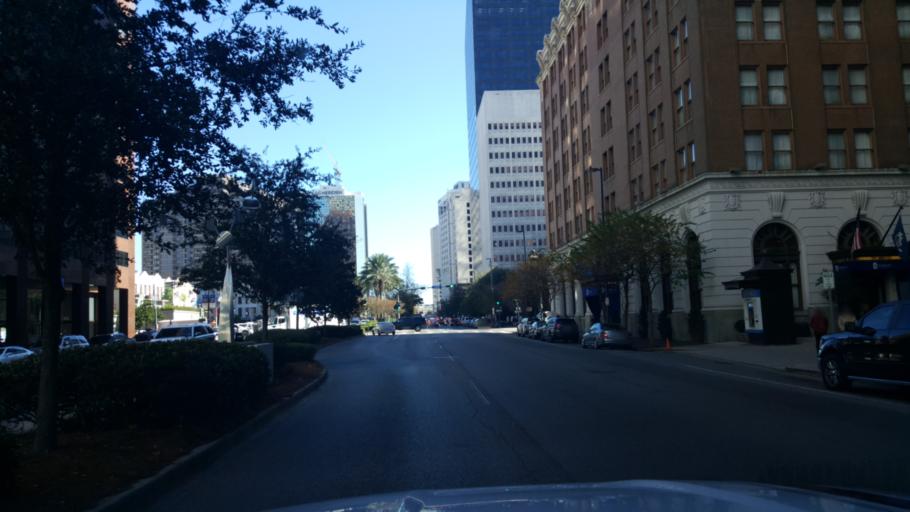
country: US
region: Louisiana
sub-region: Orleans Parish
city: New Orleans
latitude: 29.9495
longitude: -90.0703
